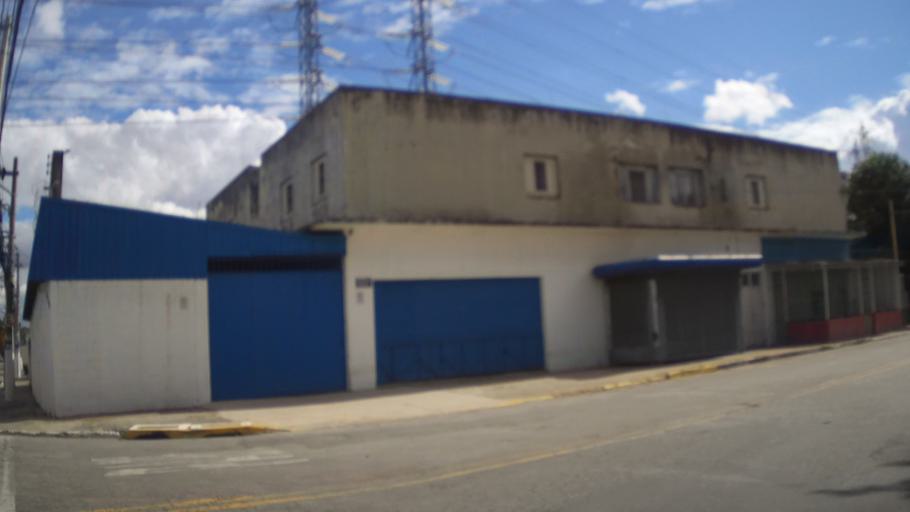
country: BR
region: Sao Paulo
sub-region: Guarulhos
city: Guarulhos
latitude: -23.4884
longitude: -46.5538
